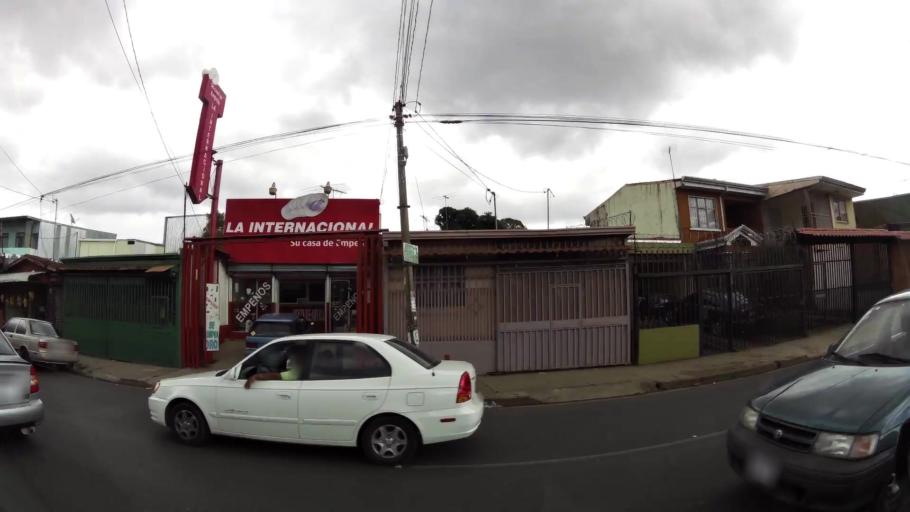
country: CR
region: San Jose
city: Alajuelita
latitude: 9.8983
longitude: -84.0870
